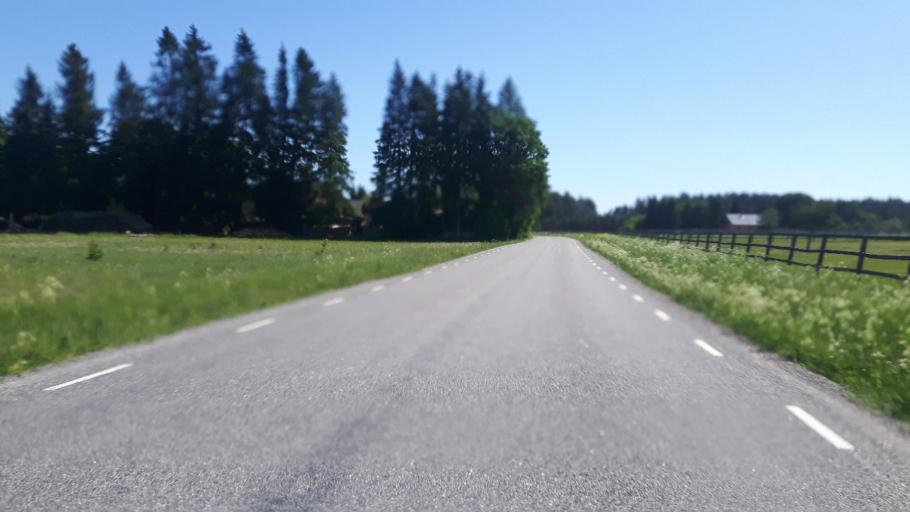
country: EE
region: Raplamaa
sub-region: Kohila vald
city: Kohila
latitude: 59.1961
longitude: 24.6979
